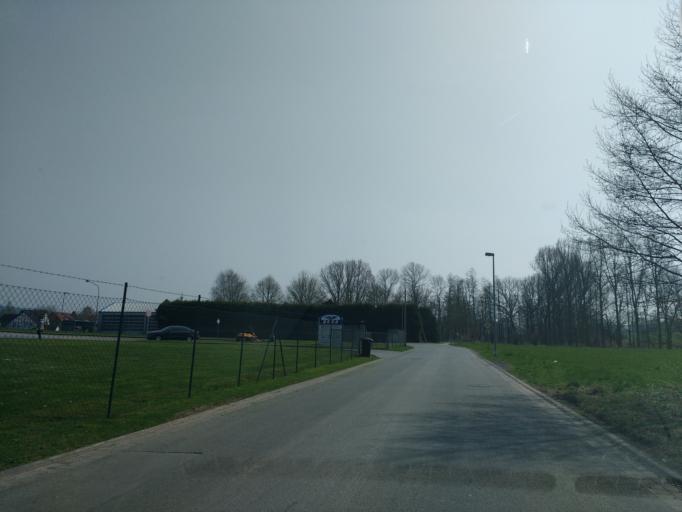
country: DE
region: North Rhine-Westphalia
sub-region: Regierungsbezirk Detmold
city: Dorentrup
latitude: 52.0255
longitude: 9.0421
